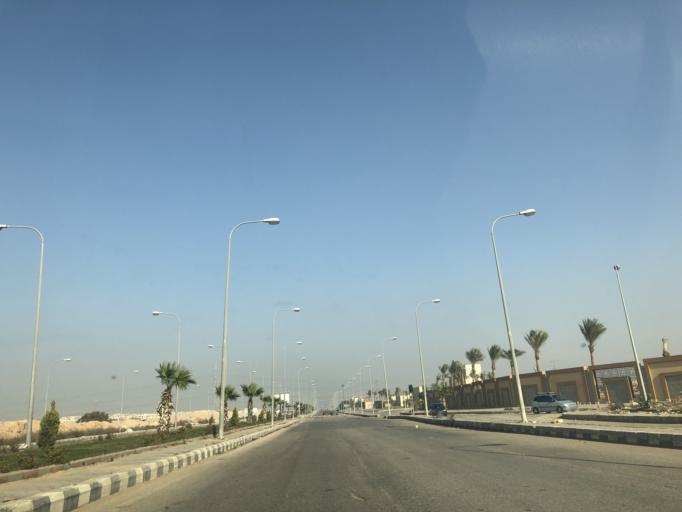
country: EG
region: Al Jizah
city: Madinat Sittah Uktubar
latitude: 29.9442
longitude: 31.0611
